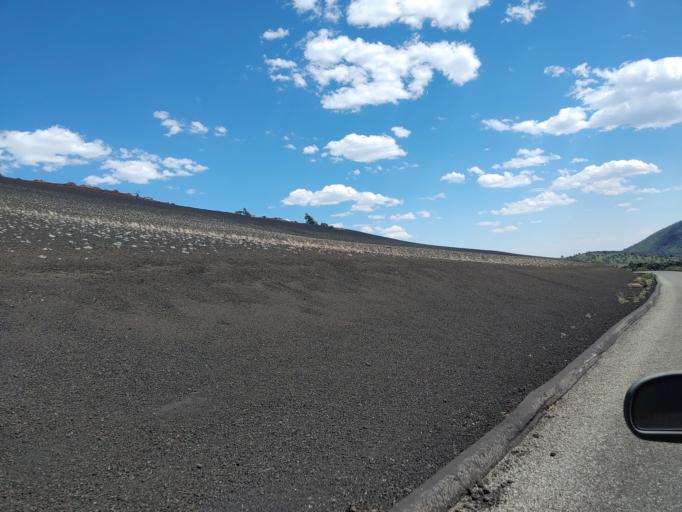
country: US
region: Idaho
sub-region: Butte County
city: Arco
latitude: 43.4427
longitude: -113.5546
